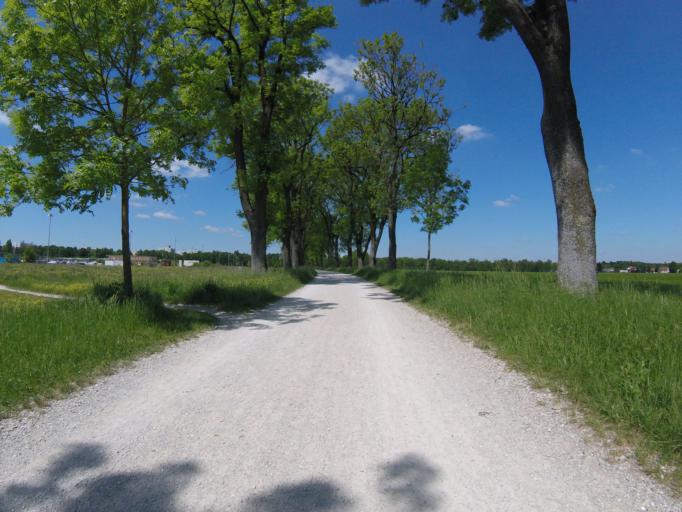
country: DE
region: Bavaria
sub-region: Upper Bavaria
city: Unterhaching
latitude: 48.0823
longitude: 11.6161
